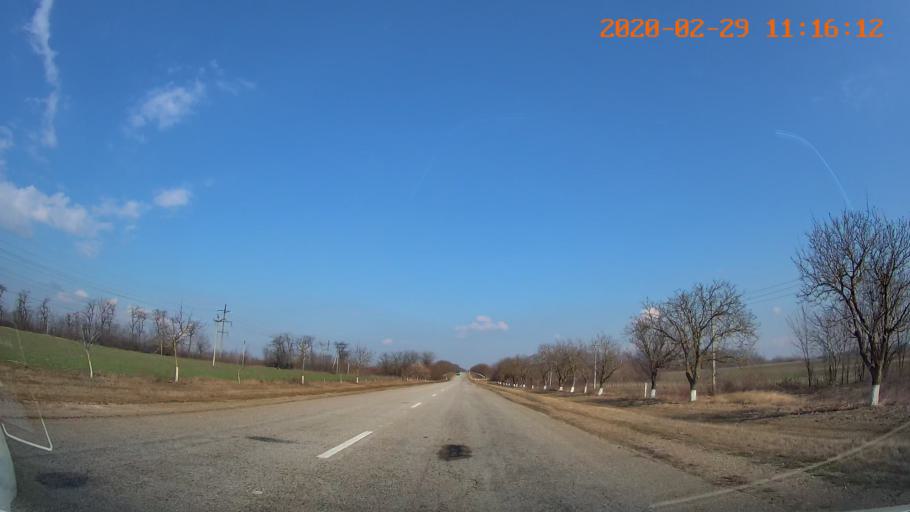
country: MD
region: Telenesti
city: Dubasari
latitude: 47.3053
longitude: 29.1672
